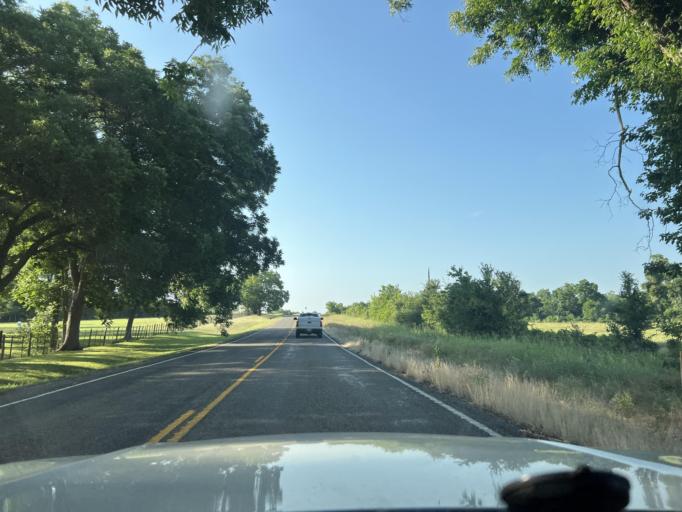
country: US
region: Texas
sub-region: Washington County
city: Brenham
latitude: 30.2288
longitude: -96.2383
